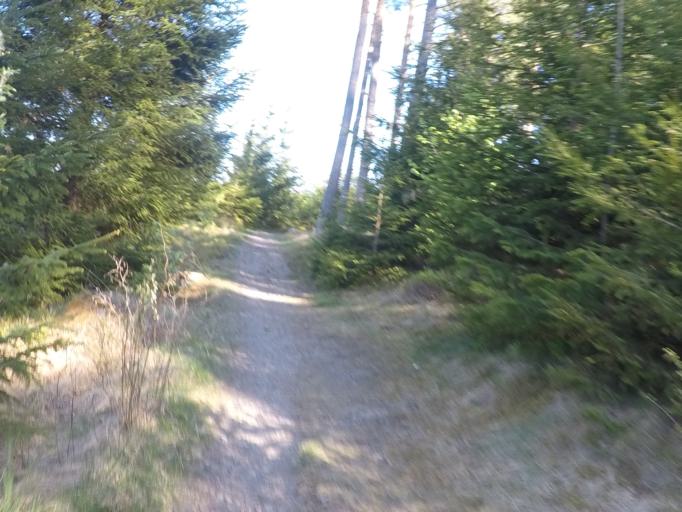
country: SE
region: Soedermanland
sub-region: Eskilstuna Kommun
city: Eskilstuna
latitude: 59.4012
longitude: 16.5407
